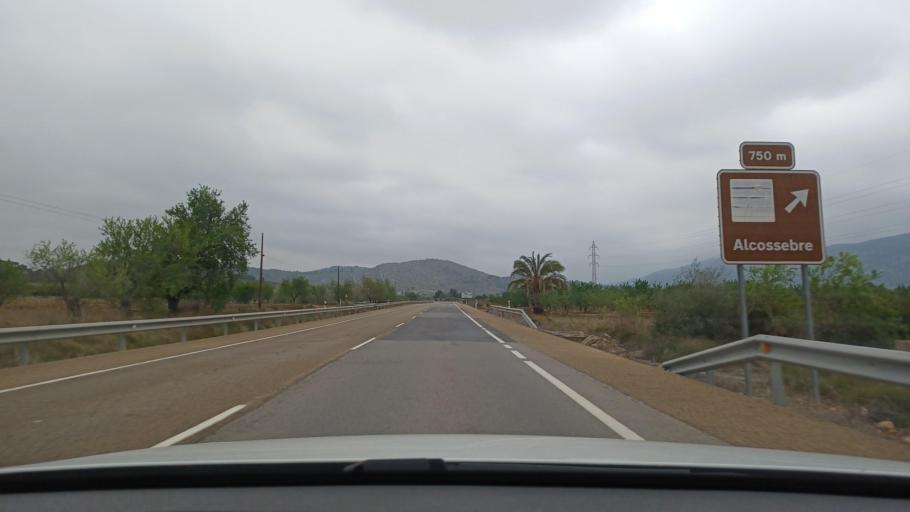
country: ES
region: Valencia
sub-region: Provincia de Castello
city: Alcala de Xivert
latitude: 40.2595
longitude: 0.2383
